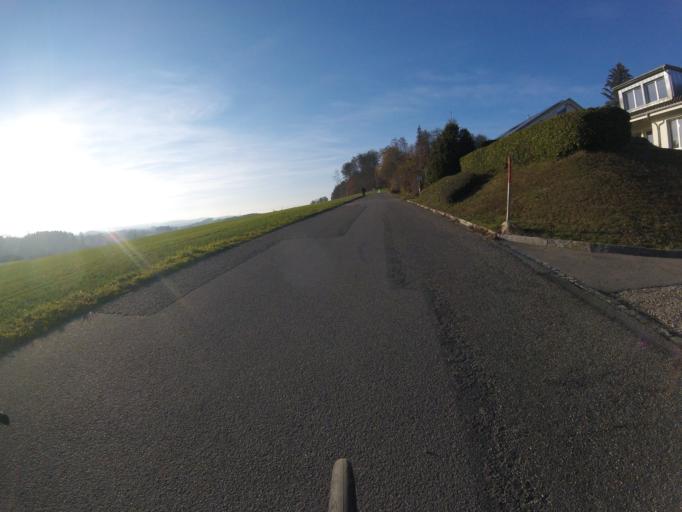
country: CH
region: Bern
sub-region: Bern-Mittelland District
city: Muhleberg
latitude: 46.9390
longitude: 7.2862
